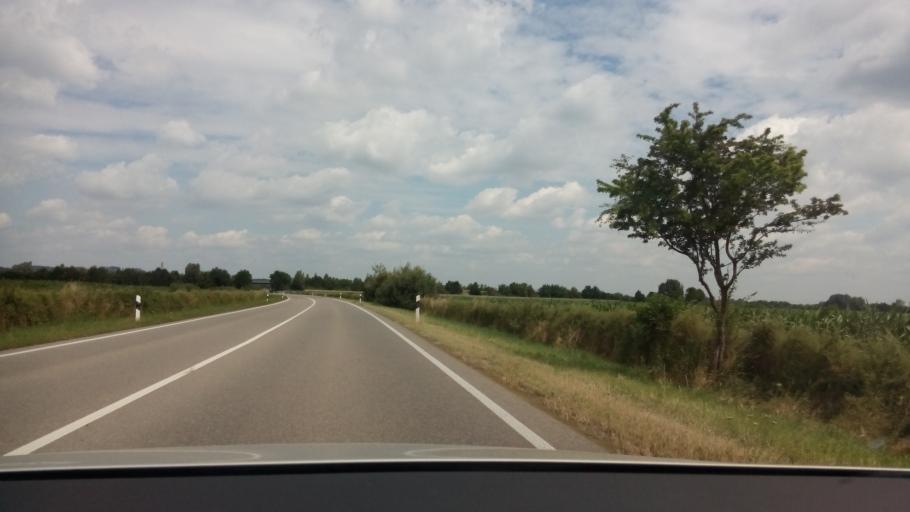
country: DE
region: Bavaria
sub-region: Upper Bavaria
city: Eitting
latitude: 48.3831
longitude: 11.8610
